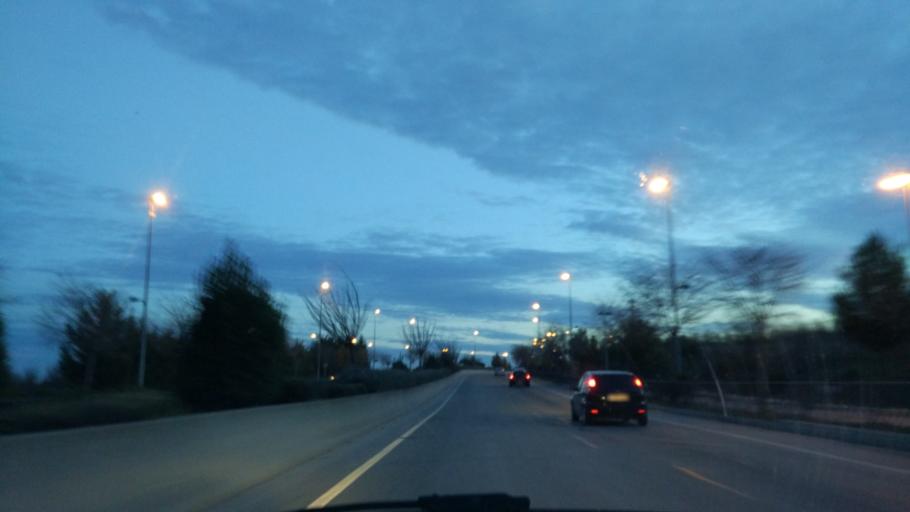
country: ES
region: Madrid
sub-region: Provincia de Madrid
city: Leganes
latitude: 40.3533
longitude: -3.7720
